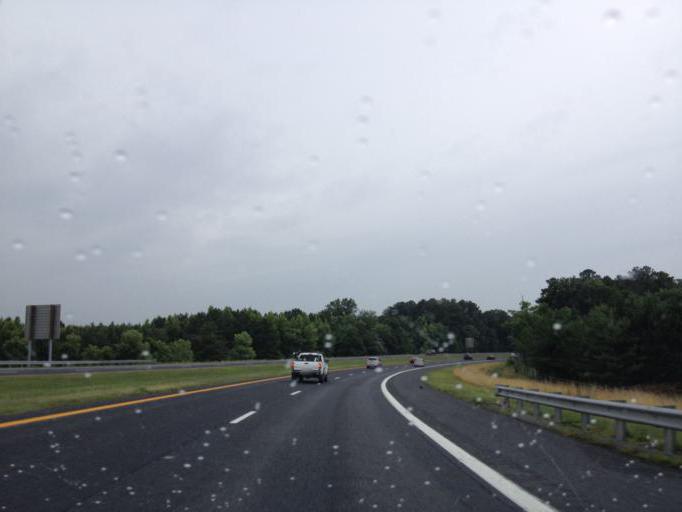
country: US
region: Maryland
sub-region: Caroline County
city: Denton
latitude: 38.8817
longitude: -75.8150
